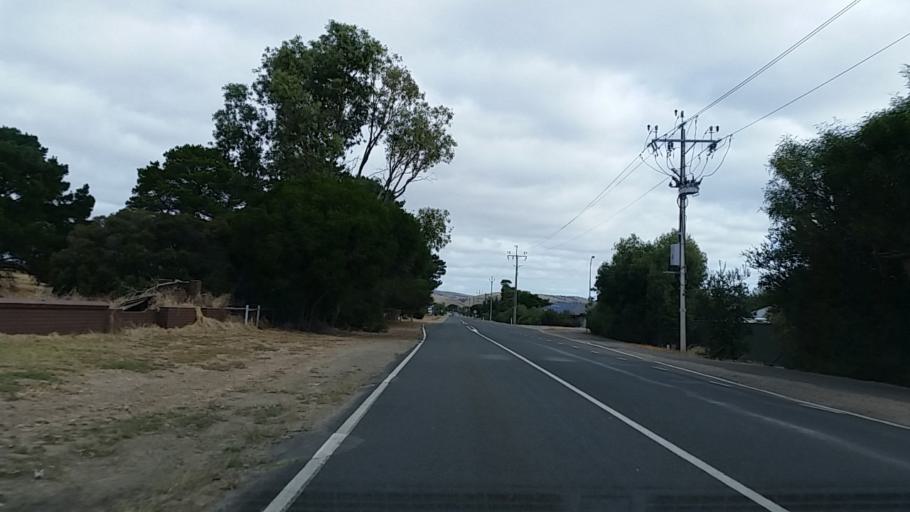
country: AU
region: South Australia
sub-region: Yankalilla
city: Normanville
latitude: -35.4347
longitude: 138.3213
